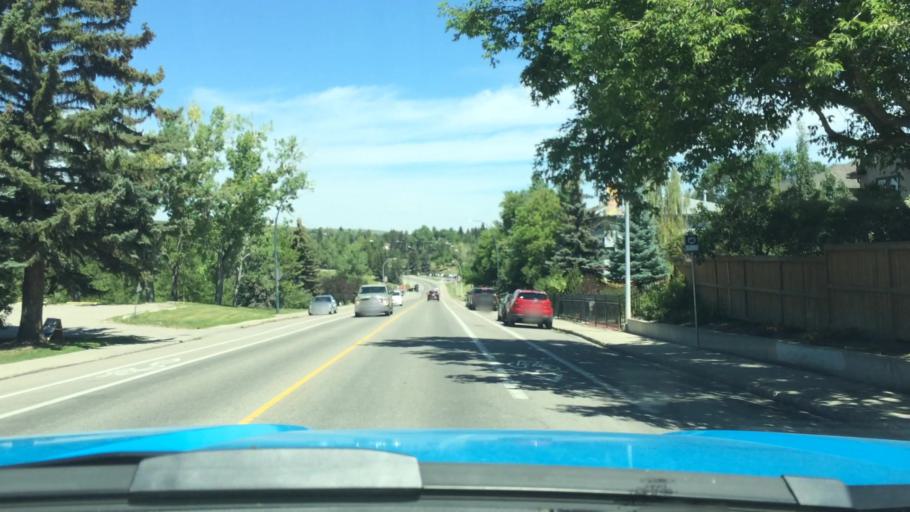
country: CA
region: Alberta
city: Calgary
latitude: 51.0734
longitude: -114.0846
